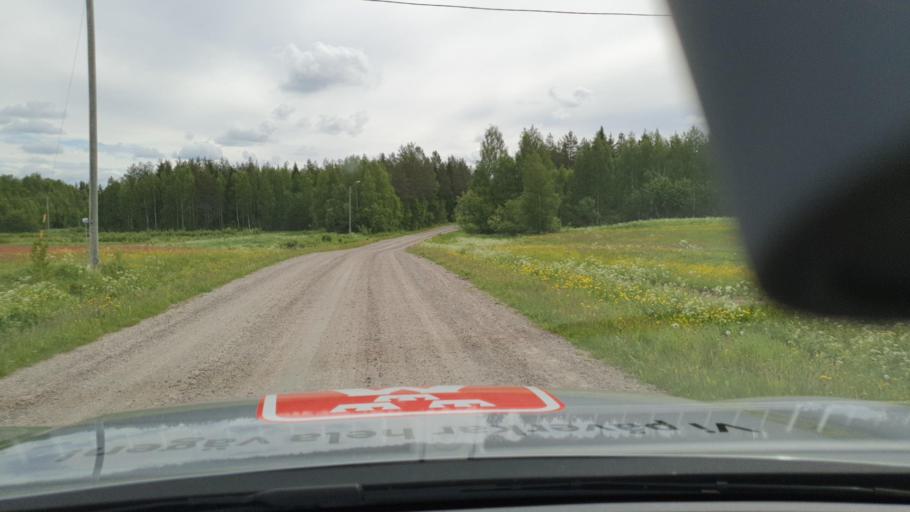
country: FI
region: Lapland
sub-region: Torniolaakso
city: Ylitornio
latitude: 65.9636
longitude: 23.6766
